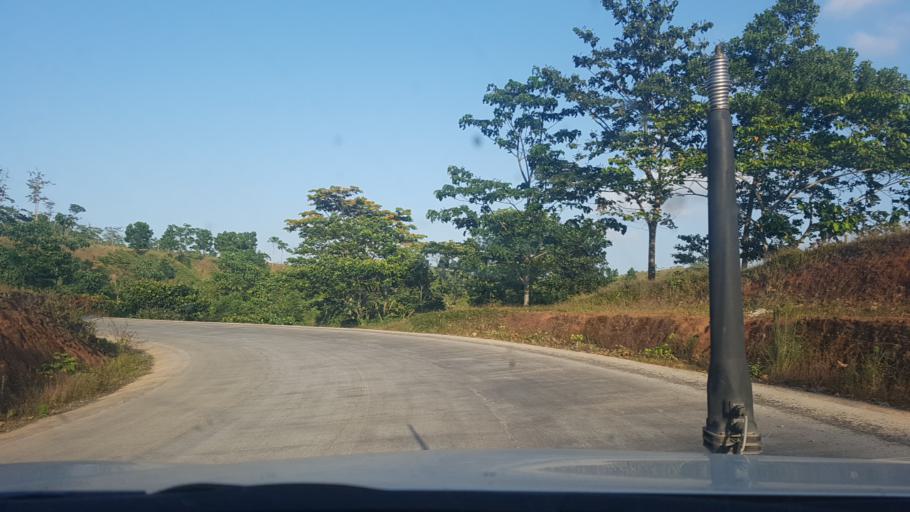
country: NI
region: Atlantico Sur
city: Nueva Guinea
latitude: 11.8053
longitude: -84.1174
